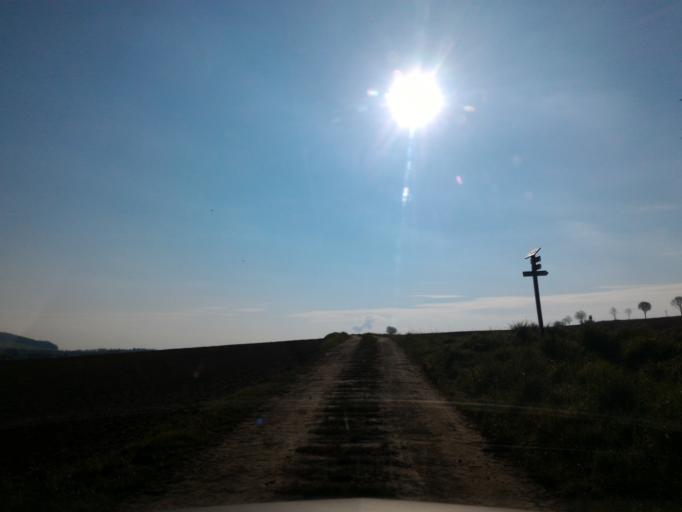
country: DE
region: Saxony
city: Leutersdorf
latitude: 50.9456
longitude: 14.6547
